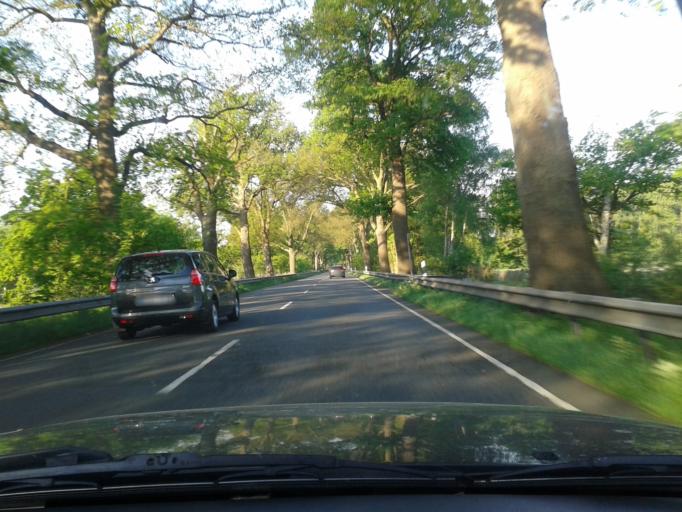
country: DE
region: Lower Saxony
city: Adelheidsdorf
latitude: 52.5316
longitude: 10.0418
